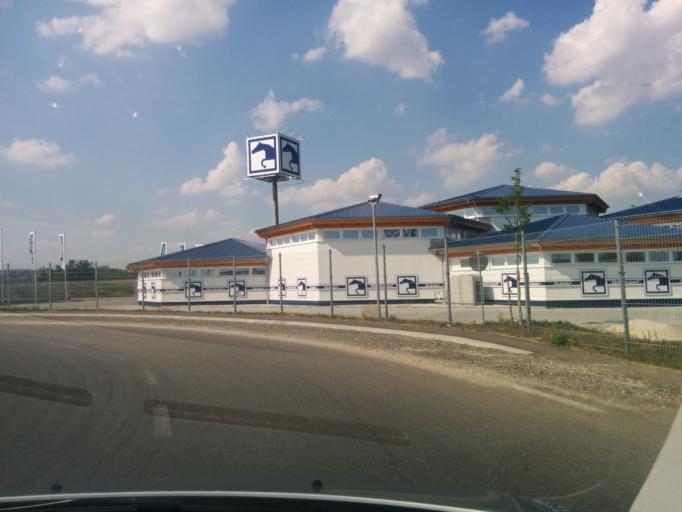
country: AT
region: Lower Austria
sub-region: Politischer Bezirk Mistelbach
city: Grossebersdorf
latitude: 48.3508
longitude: 16.4766
